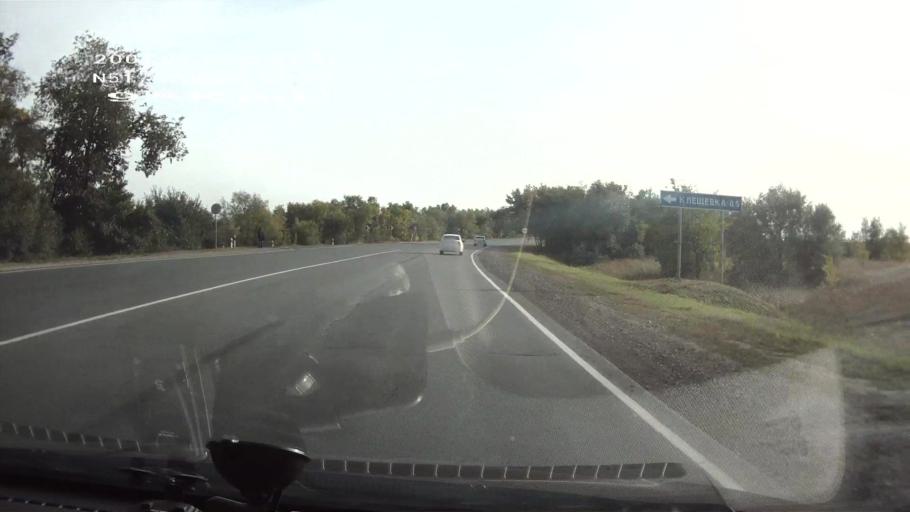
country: RU
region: Saratov
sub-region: Saratovskiy Rayon
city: Saratov
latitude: 51.7168
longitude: 46.0264
